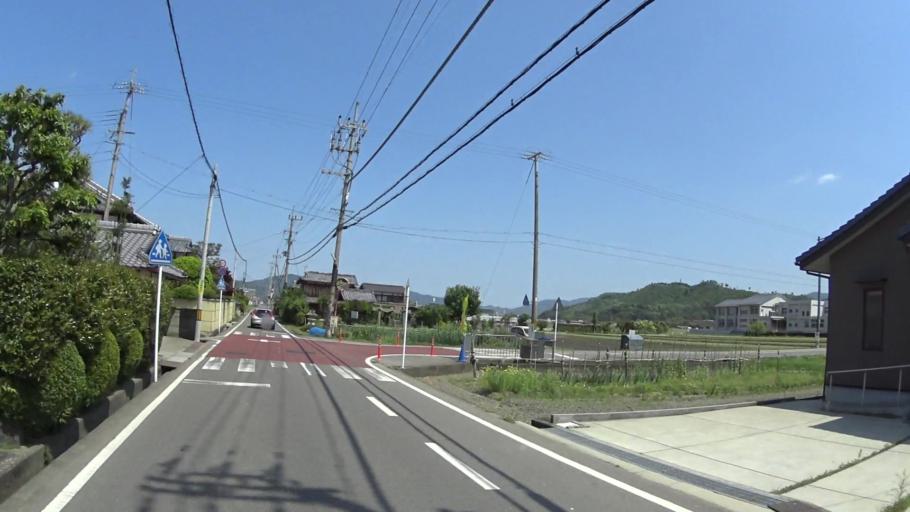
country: JP
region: Kyoto
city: Kameoka
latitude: 35.0183
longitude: 135.5560
